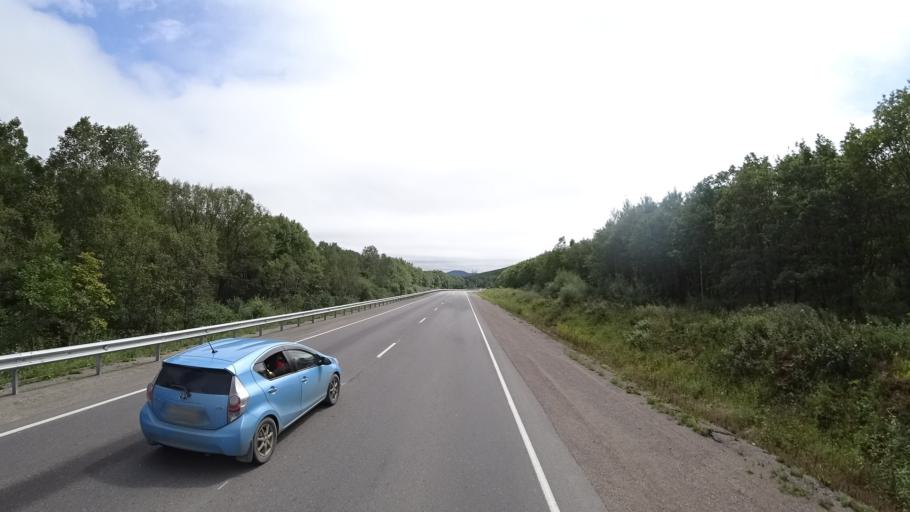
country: RU
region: Primorskiy
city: Lyalichi
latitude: 44.1139
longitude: 132.4195
